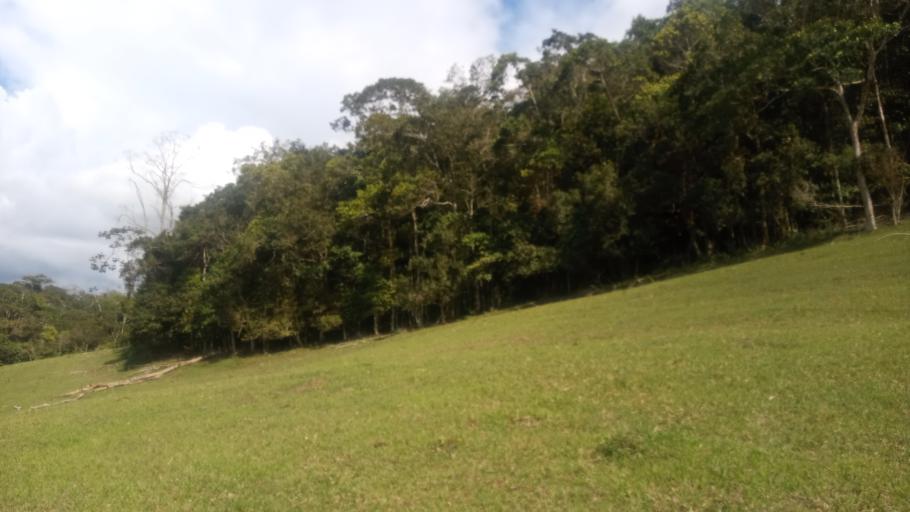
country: CO
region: Valle del Cauca
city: Yotoco
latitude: 3.8847
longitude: -76.4420
